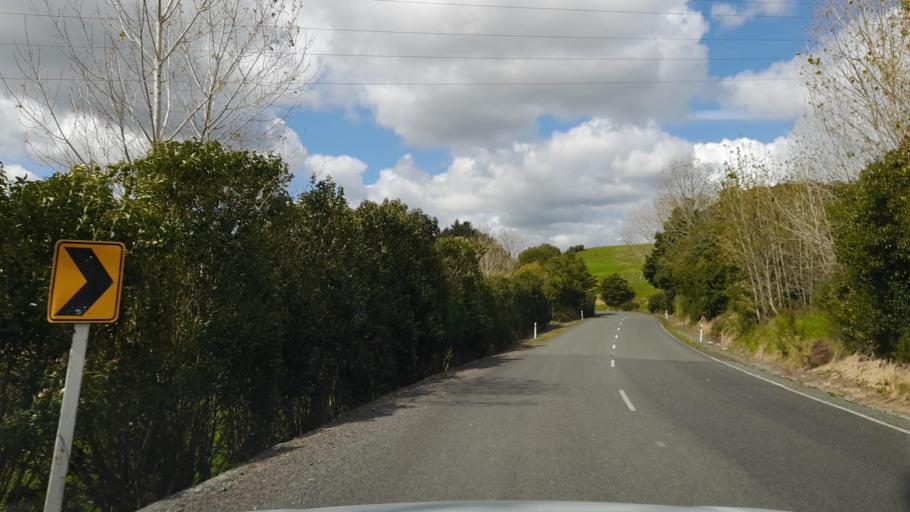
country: NZ
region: Northland
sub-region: Whangarei
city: Maungatapere
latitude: -35.6428
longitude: 174.0451
